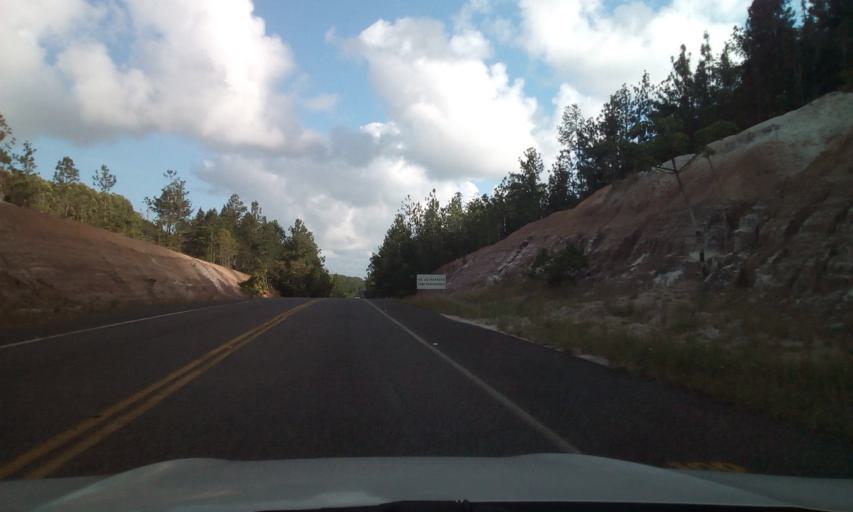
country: BR
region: Bahia
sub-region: Entre Rios
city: Entre Rios
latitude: -12.1143
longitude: -37.7865
